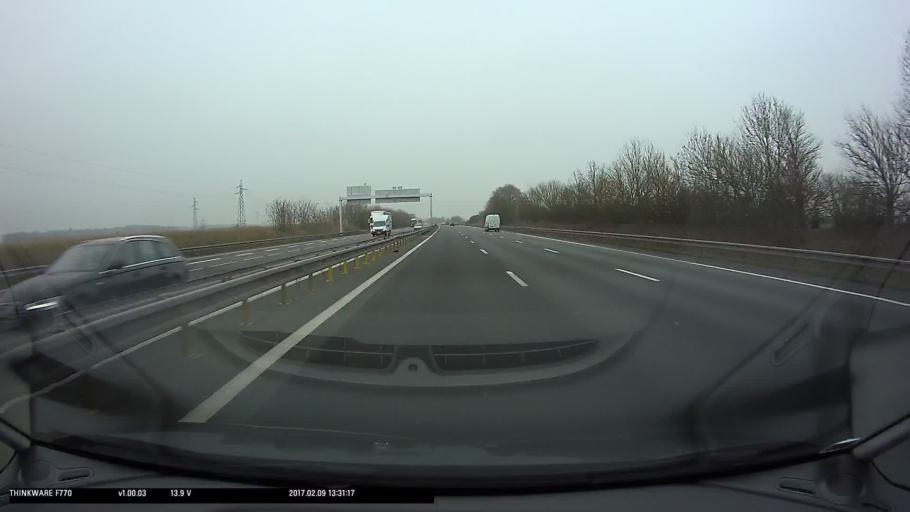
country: FR
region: Centre
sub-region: Departement du Loiret
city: Chevilly
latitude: 48.0363
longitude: 1.8402
